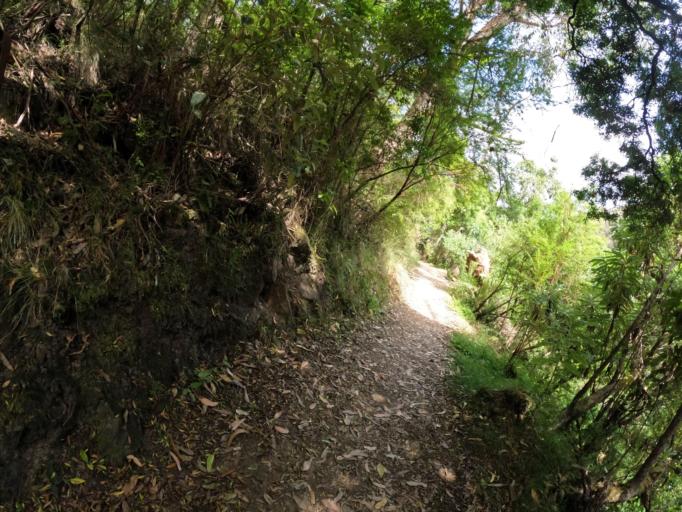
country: AU
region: Victoria
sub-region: Colac-Otway
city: Apollo Bay
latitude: -38.7904
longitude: 143.6219
